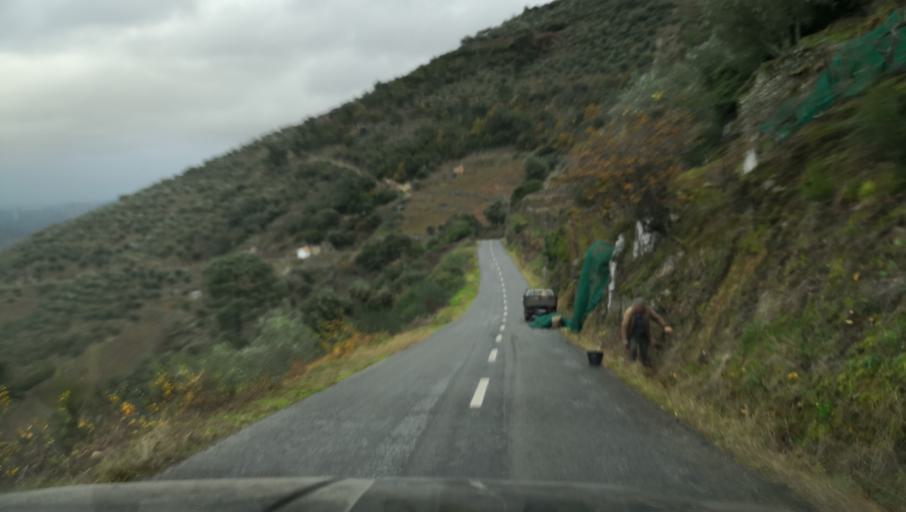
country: PT
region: Vila Real
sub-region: Santa Marta de Penaguiao
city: Santa Marta de Penaguiao
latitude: 41.2149
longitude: -7.7543
